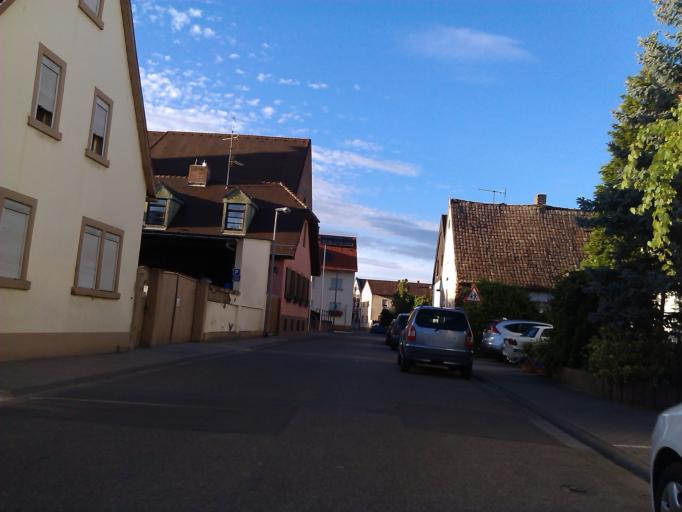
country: DE
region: Rheinland-Pfalz
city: Otterstadt
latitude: 49.3719
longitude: 8.4551
